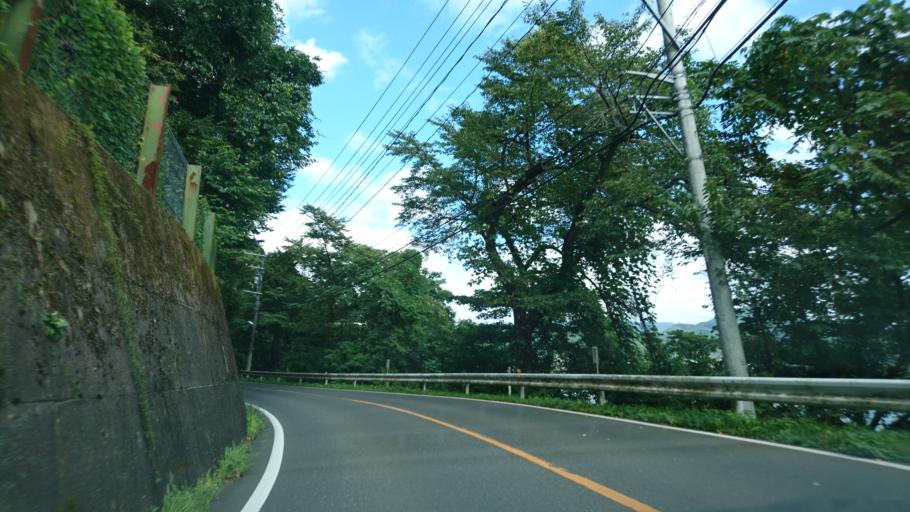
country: JP
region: Miyagi
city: Furukawa
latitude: 38.7835
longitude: 140.8496
